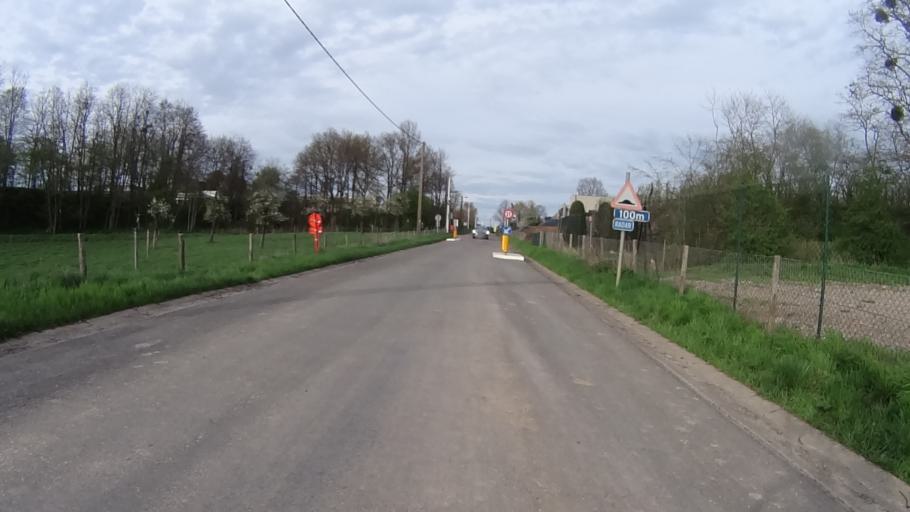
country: NL
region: Limburg
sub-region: Eijsden-Margraten
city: Eijsden
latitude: 50.7524
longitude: 5.7539
